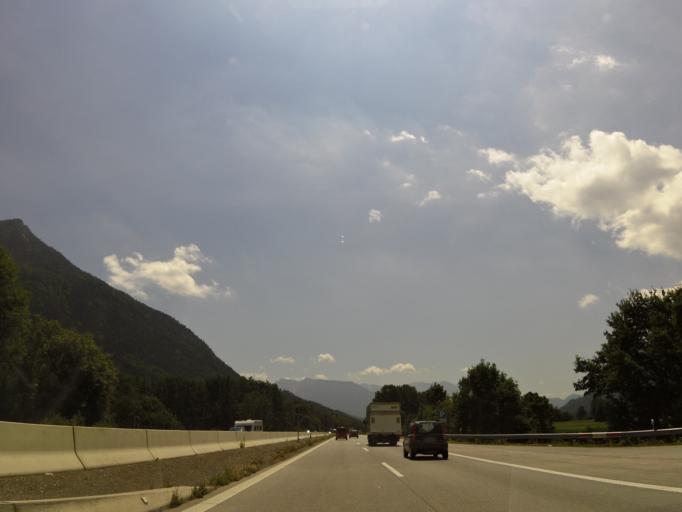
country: DE
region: Bavaria
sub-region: Upper Bavaria
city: Nussdorf am Inn
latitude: 47.7074
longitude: 12.1546
